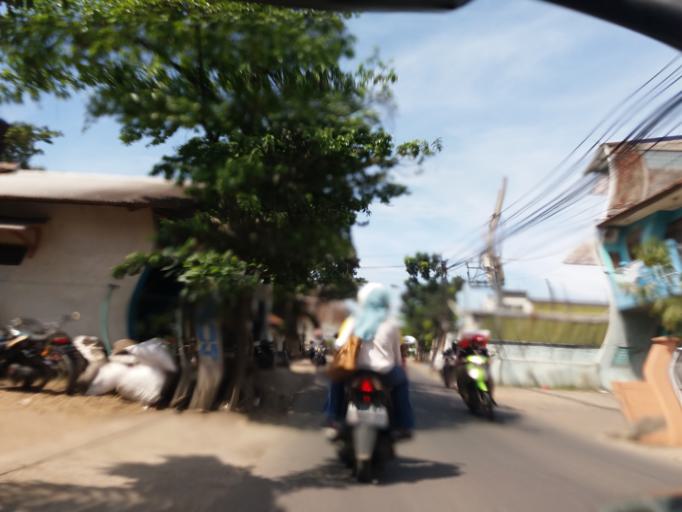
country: ID
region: West Java
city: Margahayukencana
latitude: -6.9498
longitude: 107.5703
